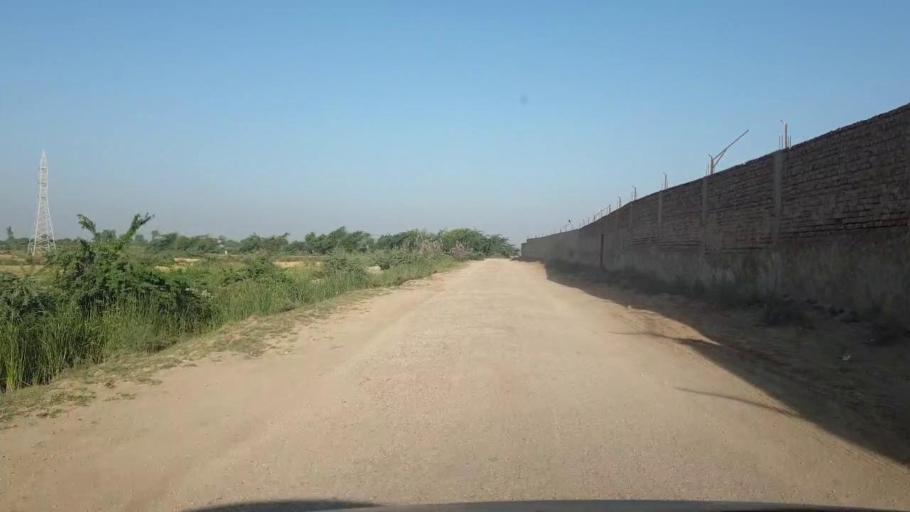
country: PK
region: Sindh
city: Badin
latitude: 24.6867
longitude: 68.8229
